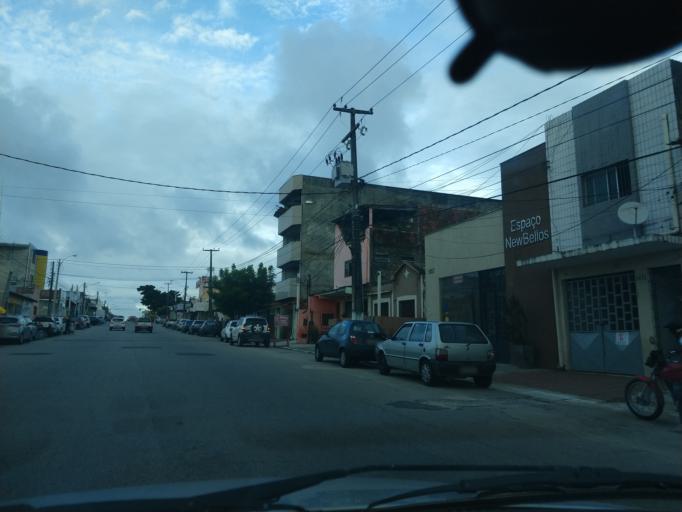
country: BR
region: Rio Grande do Norte
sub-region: Natal
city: Natal
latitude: -5.8007
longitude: -35.2226
